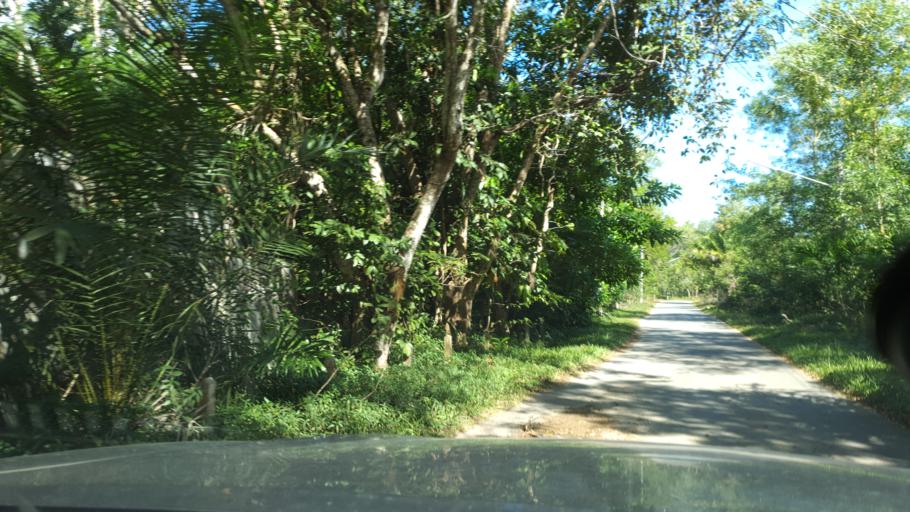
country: TH
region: Krabi
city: Krabi
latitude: 8.0236
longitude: 98.8790
